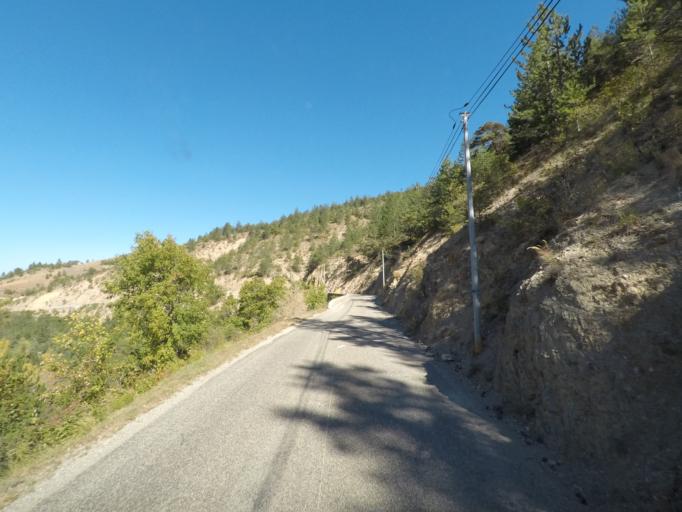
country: FR
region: Rhone-Alpes
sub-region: Departement de la Drome
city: Die
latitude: 44.6441
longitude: 5.2944
